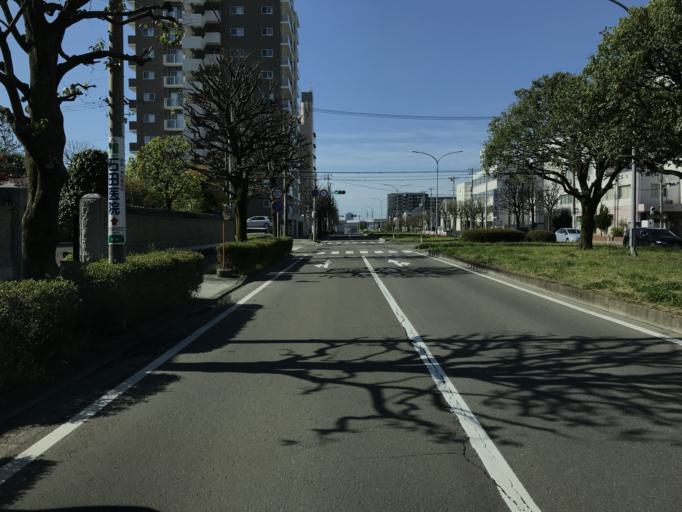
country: JP
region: Miyagi
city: Sendai-shi
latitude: 38.2549
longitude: 140.8909
